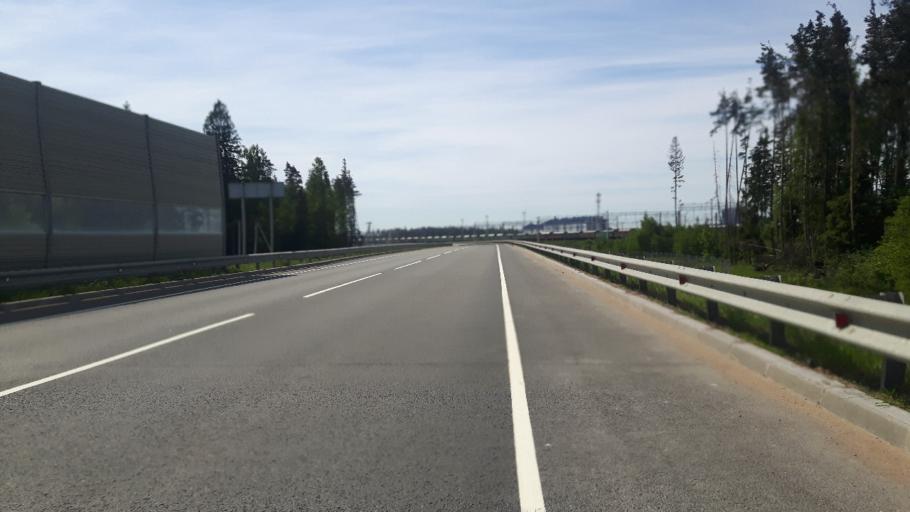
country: RU
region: Leningrad
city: Vistino
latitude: 59.6745
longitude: 28.4353
